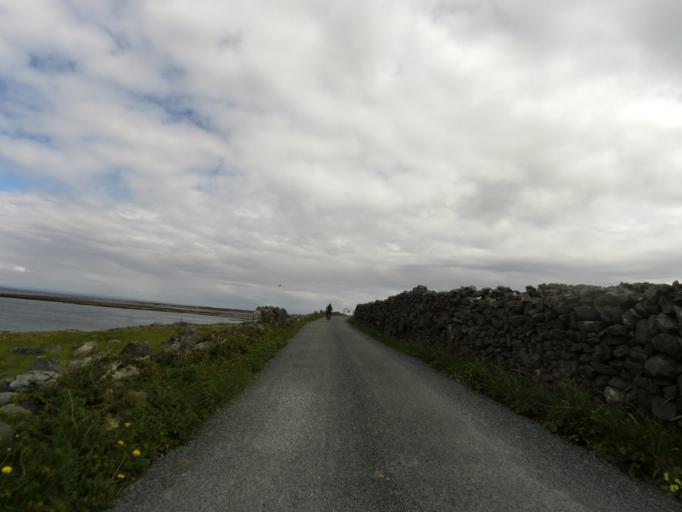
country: IE
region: Connaught
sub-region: County Galway
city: Clifden
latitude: 53.1374
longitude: -9.7154
